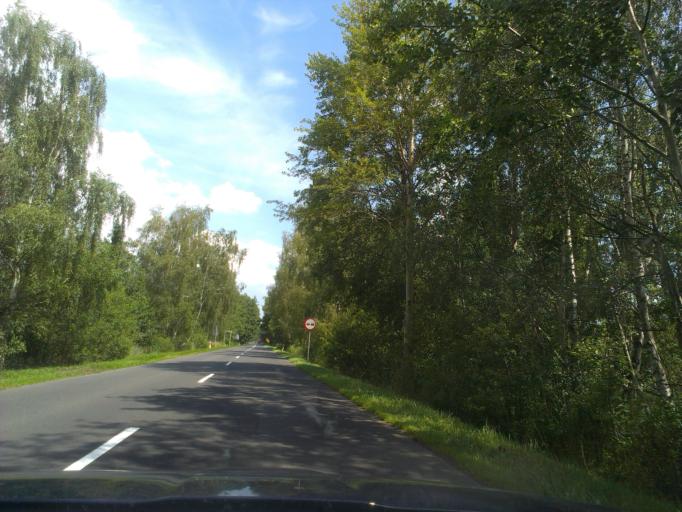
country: PL
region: West Pomeranian Voivodeship
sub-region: Swinoujscie
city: Swinoujscie
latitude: 53.8749
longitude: 14.3076
